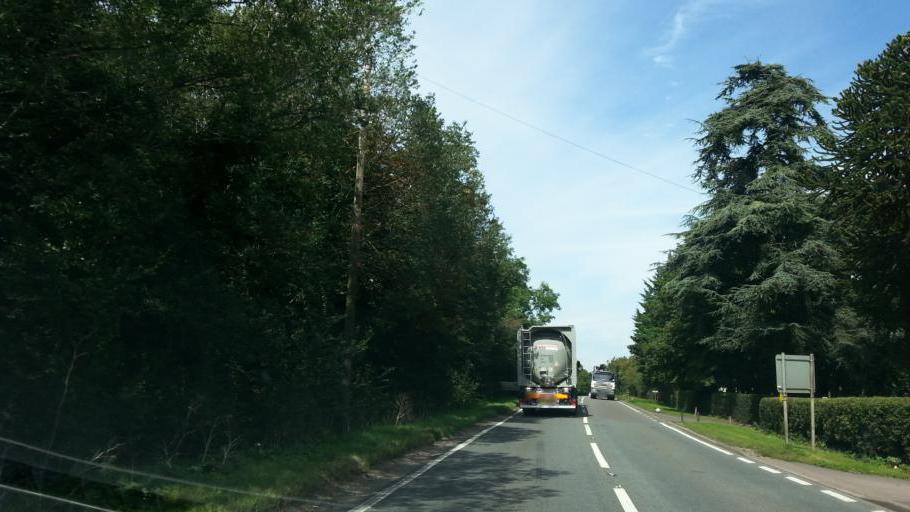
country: GB
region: England
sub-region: Suffolk
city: Exning
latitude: 52.2807
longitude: 0.3935
